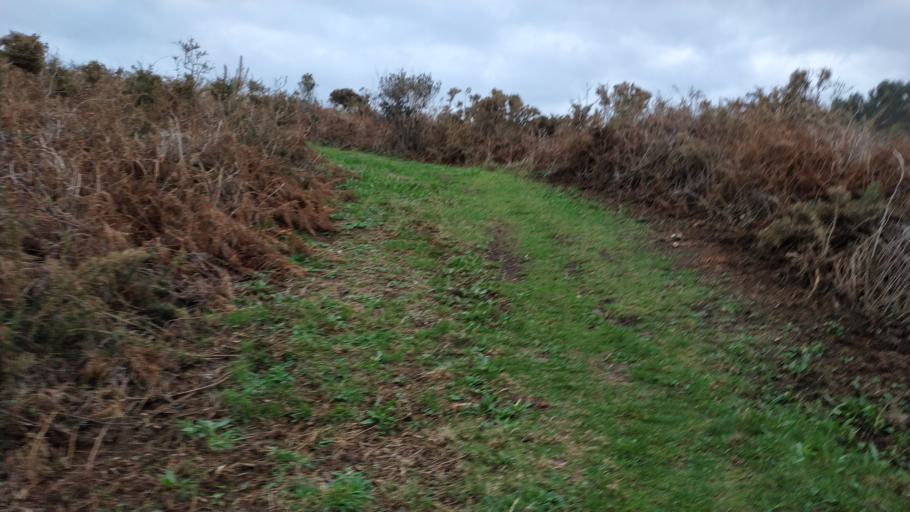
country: ES
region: Galicia
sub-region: Provincia da Coruna
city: Oleiros
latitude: 43.4008
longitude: -8.3303
